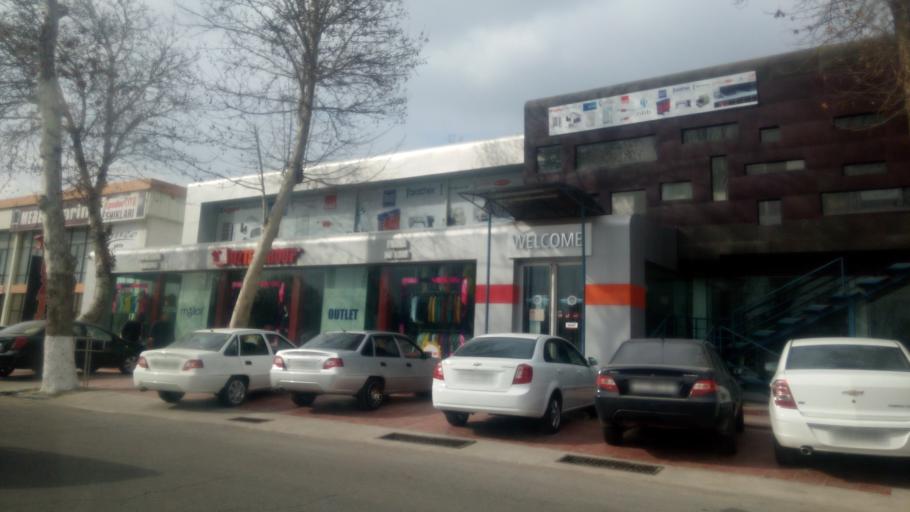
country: UZ
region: Toshkent Shahri
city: Tashkent
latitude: 41.3480
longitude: 69.2496
